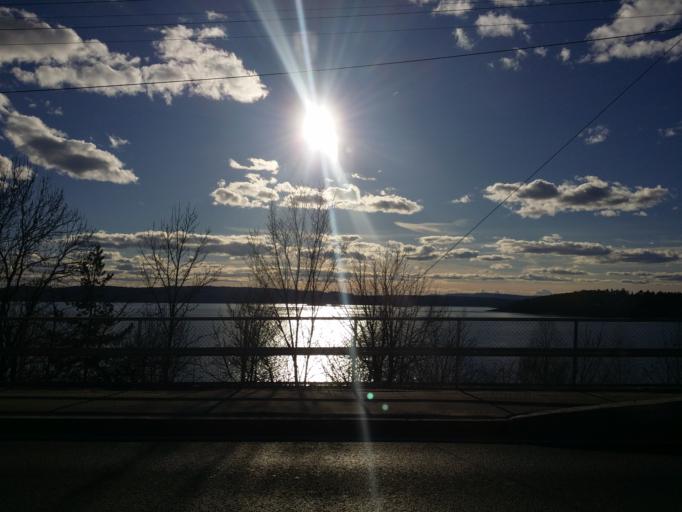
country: NO
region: Akershus
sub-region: Oppegard
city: Kolbotn
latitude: 59.8616
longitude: 10.7849
